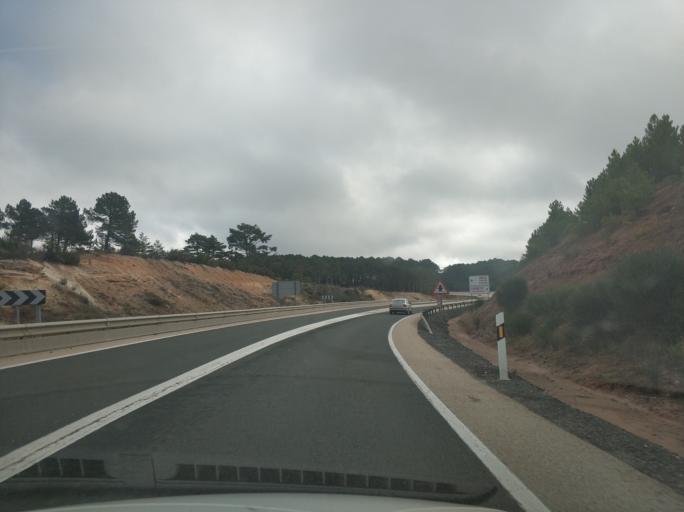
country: ES
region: Castille and Leon
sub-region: Provincia de Soria
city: Navaleno
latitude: 41.8280
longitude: -2.9549
